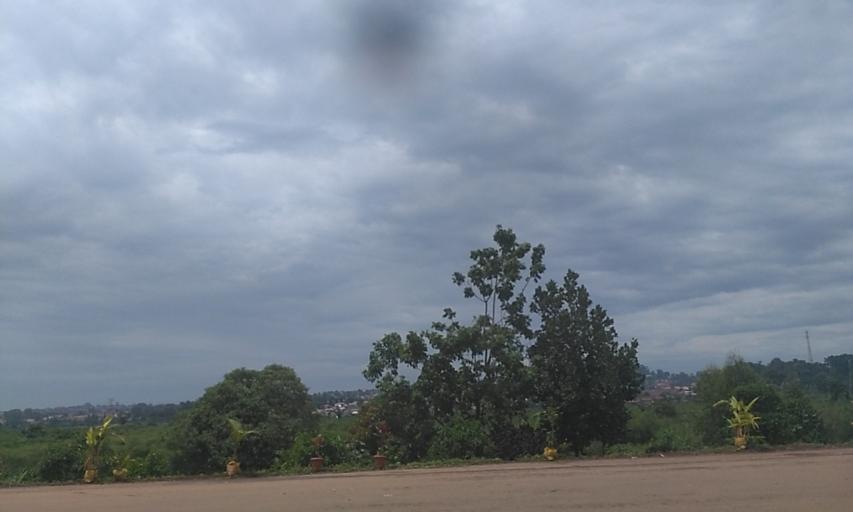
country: UG
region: Central Region
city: Kampala Central Division
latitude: 0.3255
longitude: 32.5237
